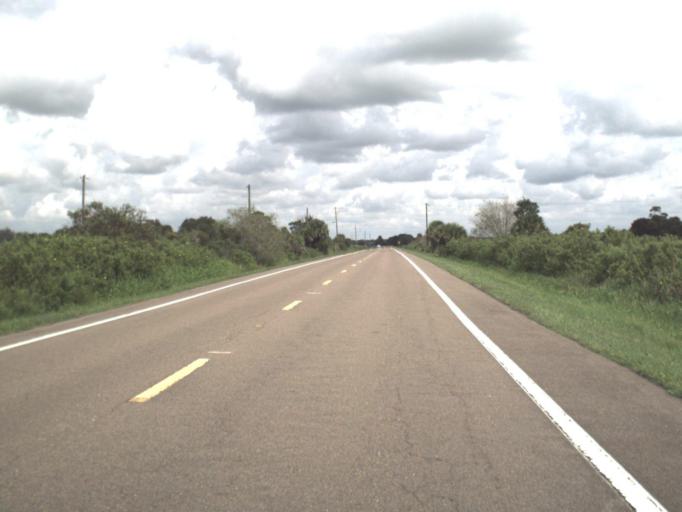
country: US
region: Florida
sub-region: Sarasota County
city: North Port
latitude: 27.1934
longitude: -82.0974
